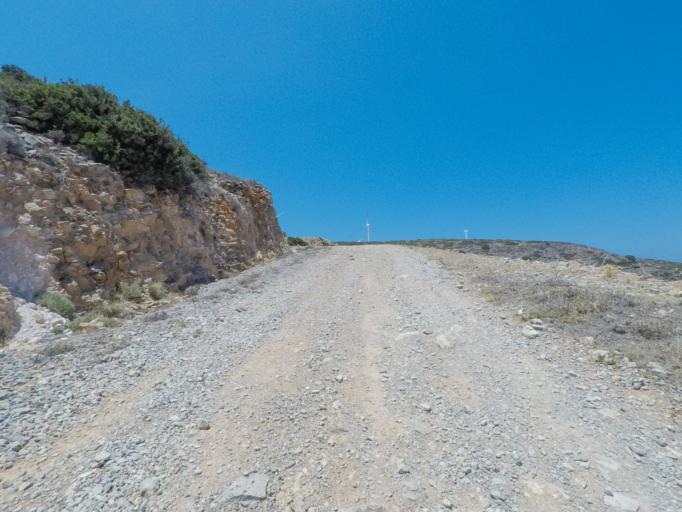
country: GR
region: Crete
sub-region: Nomos Lasithiou
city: Elounda
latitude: 35.3269
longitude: 25.7612
